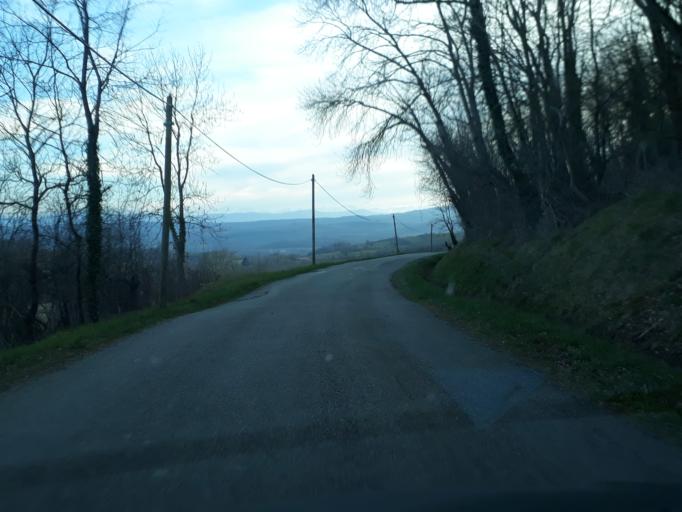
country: FR
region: Midi-Pyrenees
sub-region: Departement de la Haute-Garonne
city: Montesquieu-Volvestre
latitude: 43.1707
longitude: 1.3206
